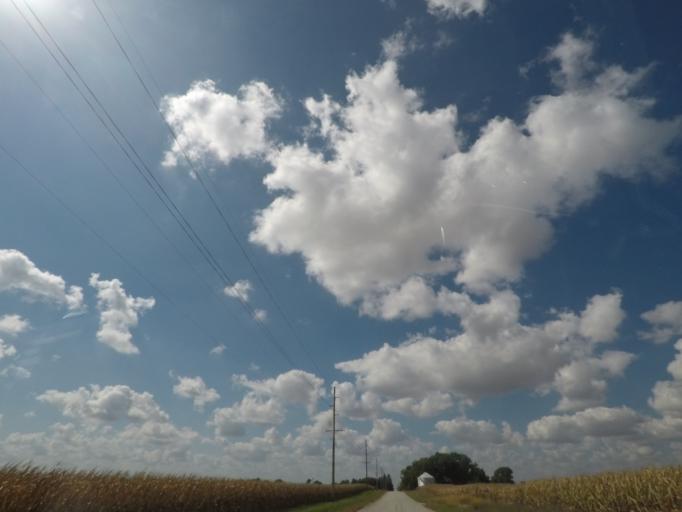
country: US
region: Iowa
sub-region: Story County
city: Nevada
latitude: 42.0343
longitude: -93.3886
